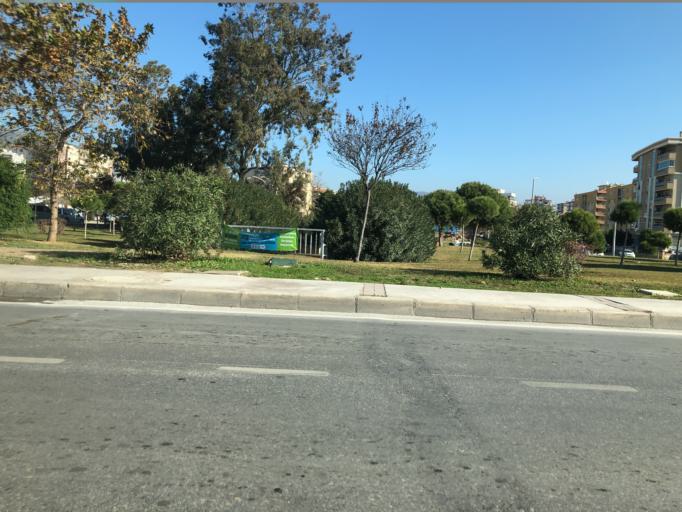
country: TR
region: Izmir
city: Izmir
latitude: 38.4618
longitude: 27.1718
